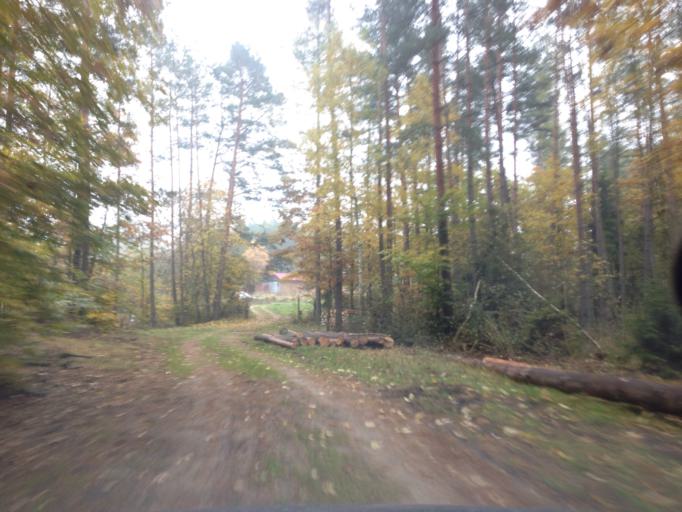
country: PL
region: Kujawsko-Pomorskie
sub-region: Powiat brodnicki
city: Gorzno
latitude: 53.2195
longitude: 19.7192
